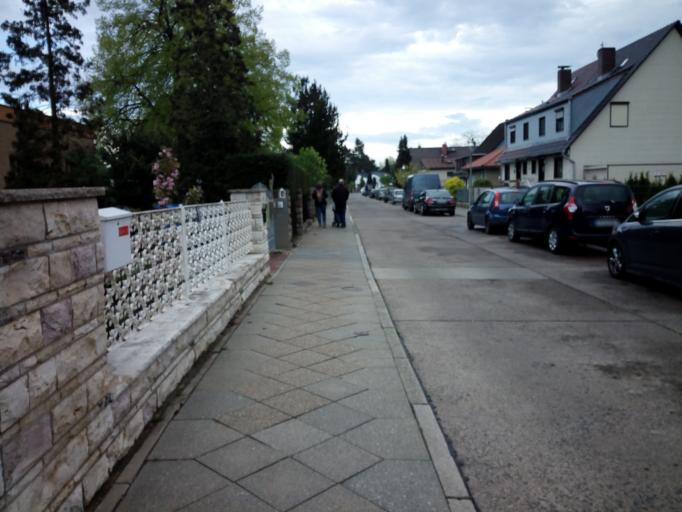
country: DE
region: Berlin
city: Rudow
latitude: 52.4255
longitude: 13.4978
